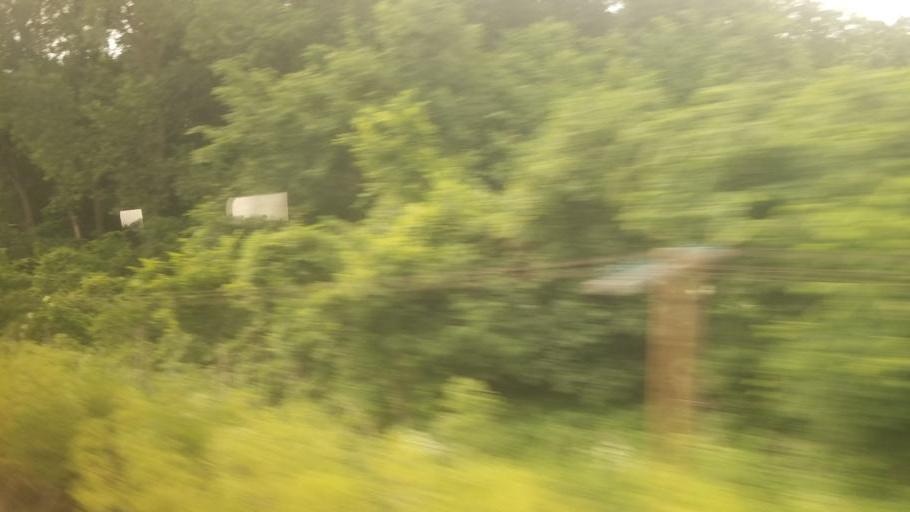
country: US
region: Kansas
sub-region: Jefferson County
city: Oskaloosa
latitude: 39.0610
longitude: -95.4275
